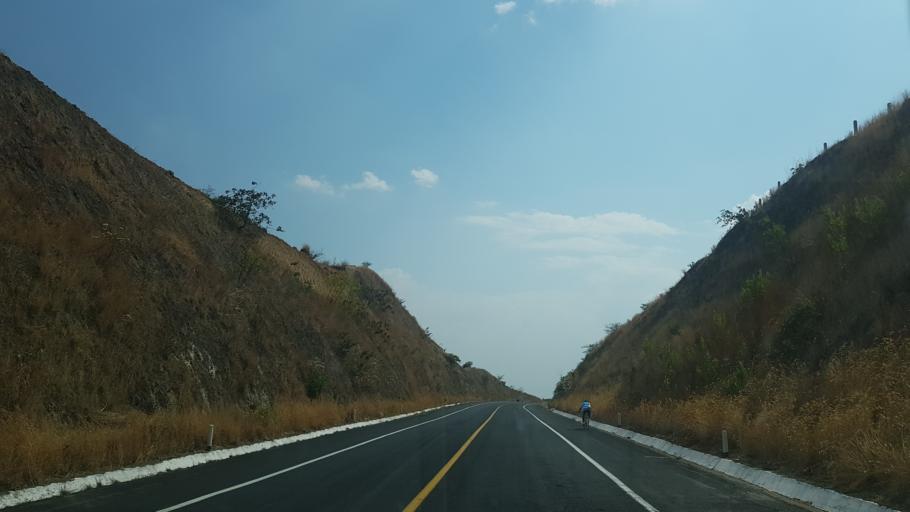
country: MX
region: Morelos
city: Tlacotepec
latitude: 18.8017
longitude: -98.7085
